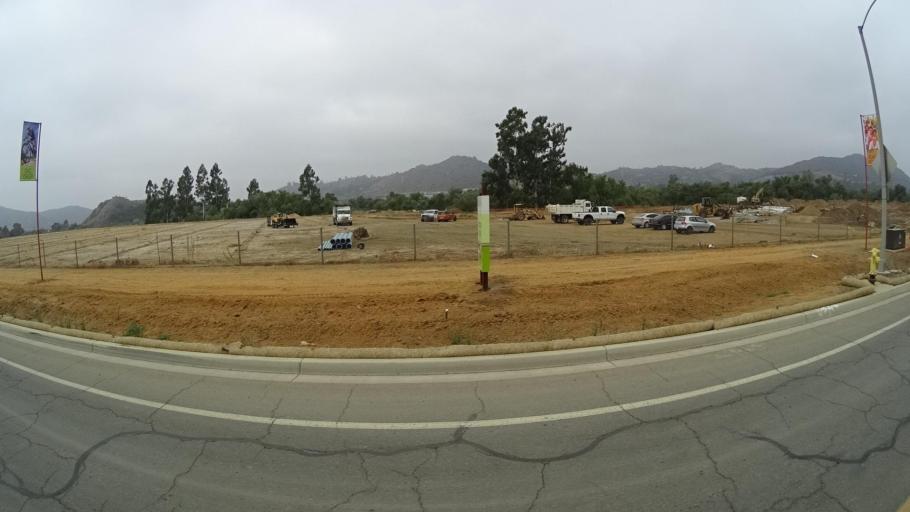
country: US
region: California
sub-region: San Diego County
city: Rainbow
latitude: 33.3397
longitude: -117.1479
